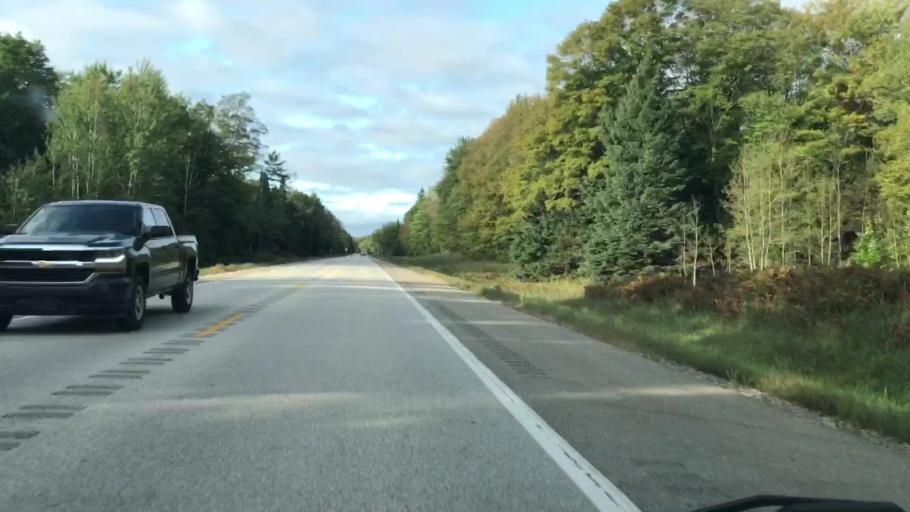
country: US
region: Michigan
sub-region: Luce County
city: Newberry
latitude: 46.3392
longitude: -85.0420
